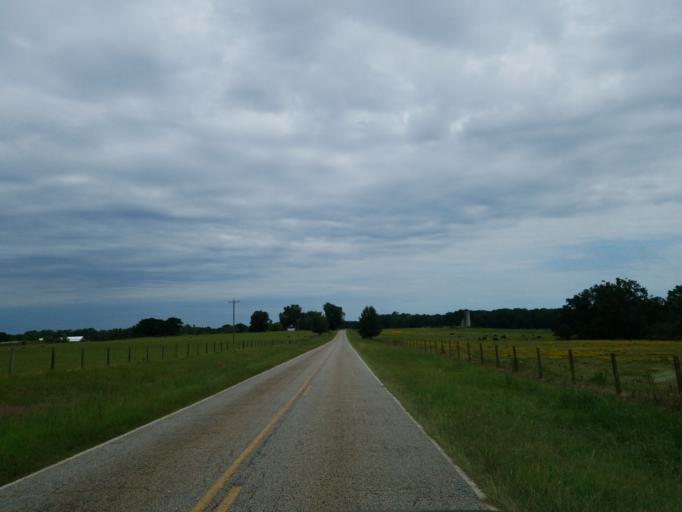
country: US
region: Georgia
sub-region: Lamar County
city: Barnesville
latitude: 33.0003
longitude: -84.0572
